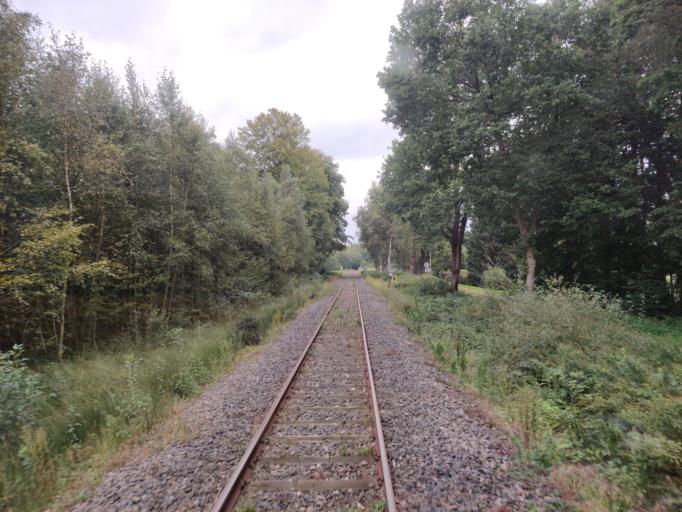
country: DE
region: Lower Saxony
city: Gnarrenburg
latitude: 53.4031
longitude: 9.0115
